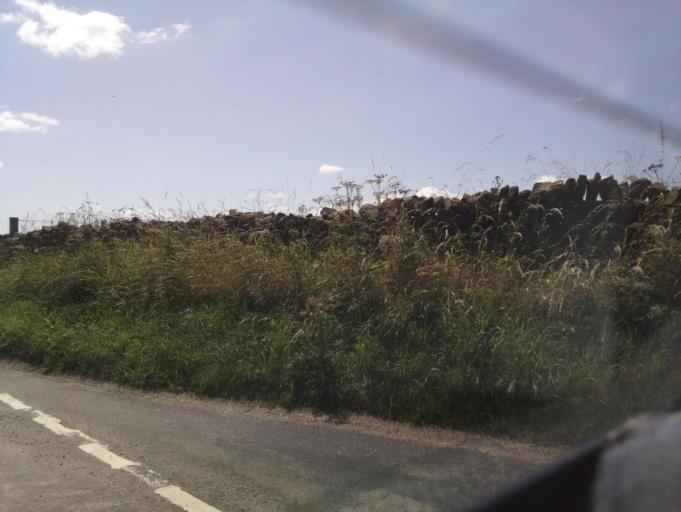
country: GB
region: England
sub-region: Derbyshire
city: Buxton
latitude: 53.1877
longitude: -1.8763
